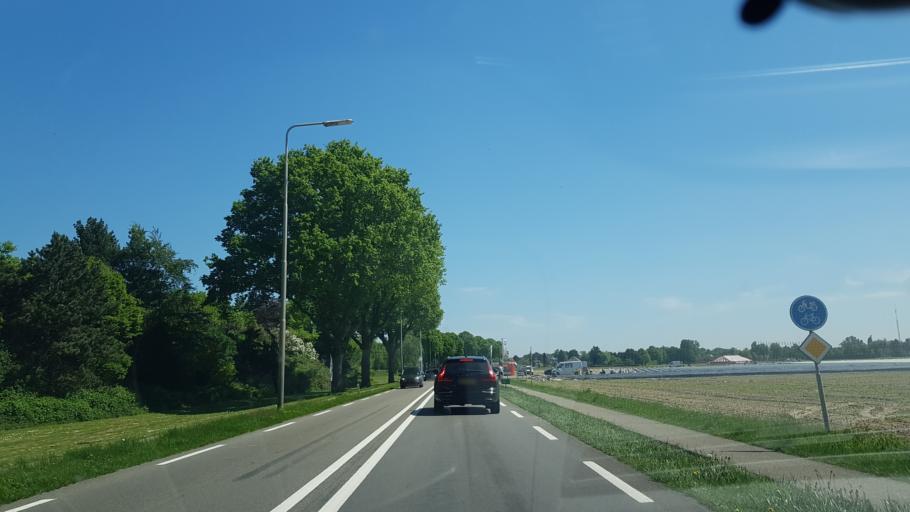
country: NL
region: Limburg
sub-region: Gemeente Leudal
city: Heythuysen
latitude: 51.2235
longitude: 5.8733
